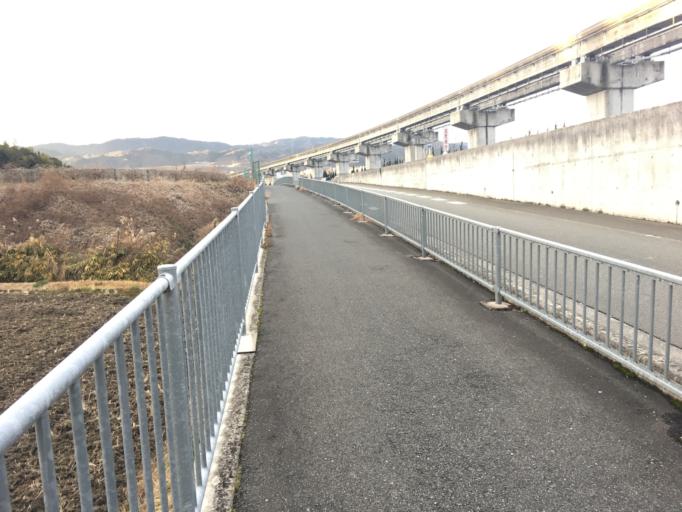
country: JP
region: Osaka
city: Ibaraki
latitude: 34.8395
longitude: 135.5257
